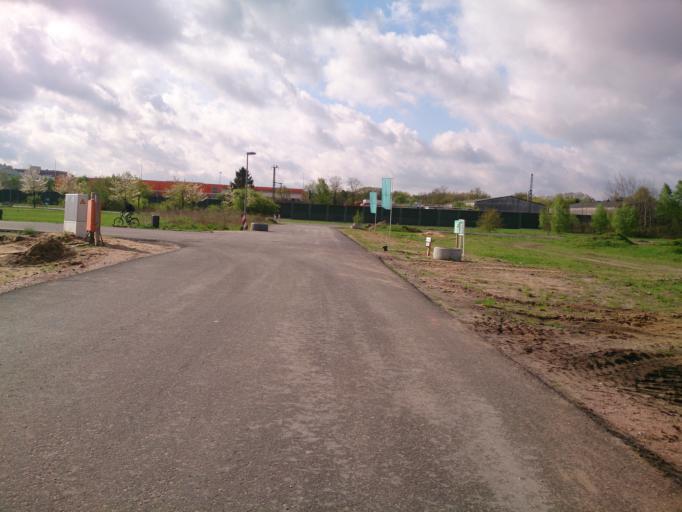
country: DE
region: Lower Saxony
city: Neu Wulmstorf
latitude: 53.4759
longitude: 9.8462
